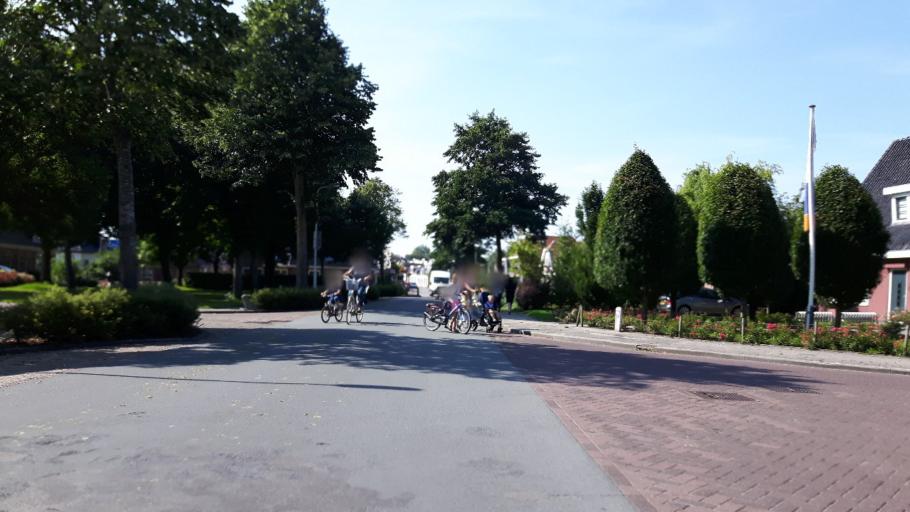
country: NL
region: Friesland
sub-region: Gemeente Ferwerderadiel
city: Ferwert
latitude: 53.3404
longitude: 5.8278
